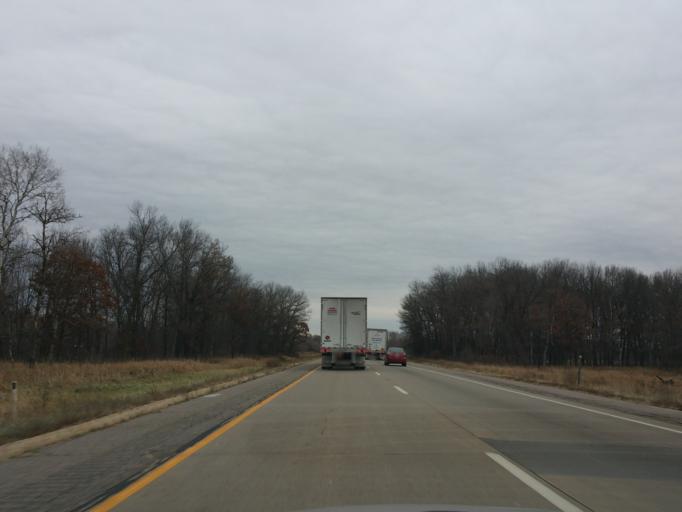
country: US
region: Wisconsin
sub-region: Juneau County
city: New Lisbon
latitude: 43.8543
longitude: -90.1087
